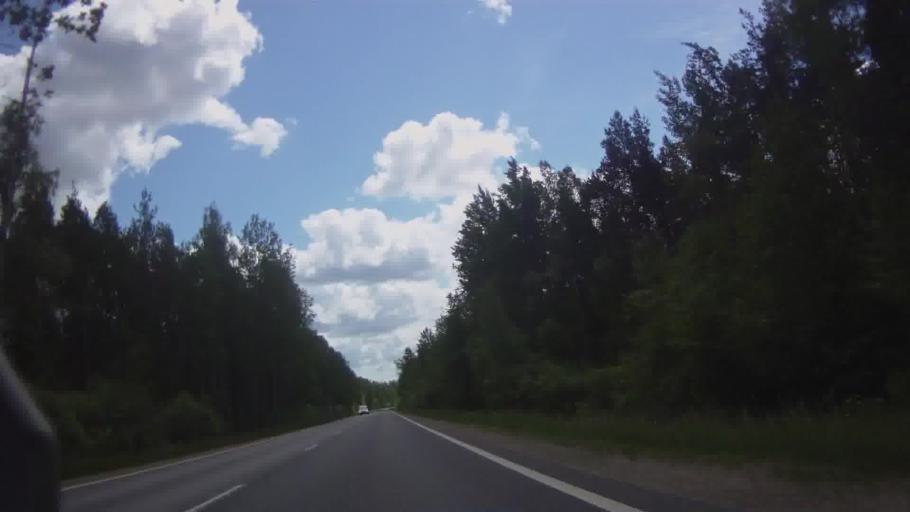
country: LV
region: Livani
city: Livani
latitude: 56.5380
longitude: 26.1322
